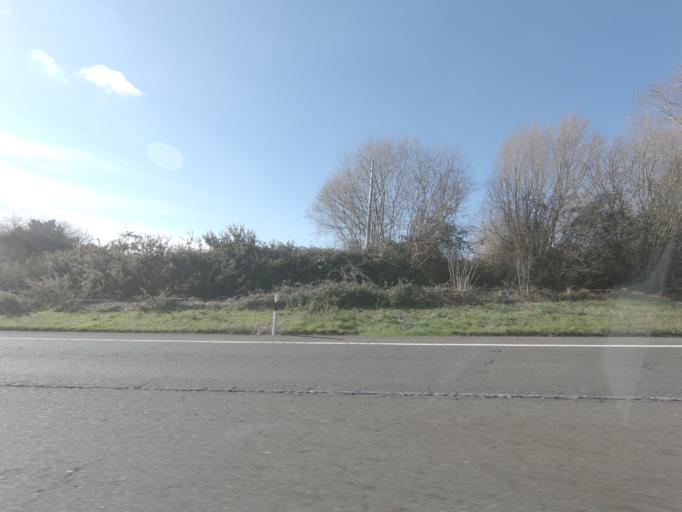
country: ES
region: Galicia
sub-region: Provincia da Coruna
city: Ribeira
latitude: 42.7101
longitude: -8.3852
